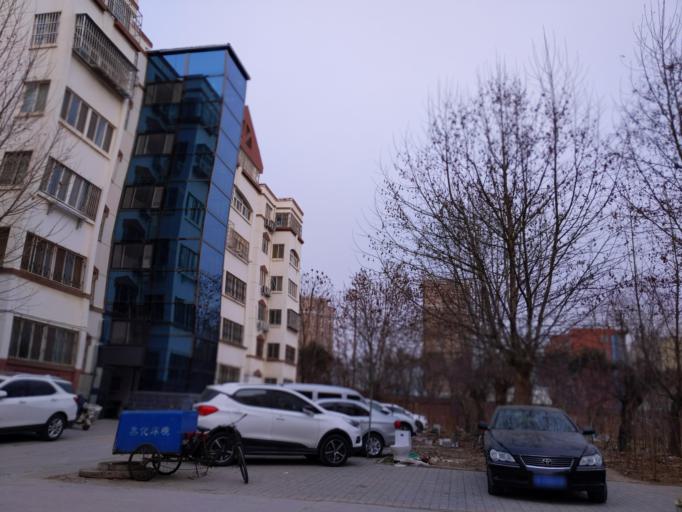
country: CN
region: Henan Sheng
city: Zhongyuanlu
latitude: 35.7552
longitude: 115.0543
